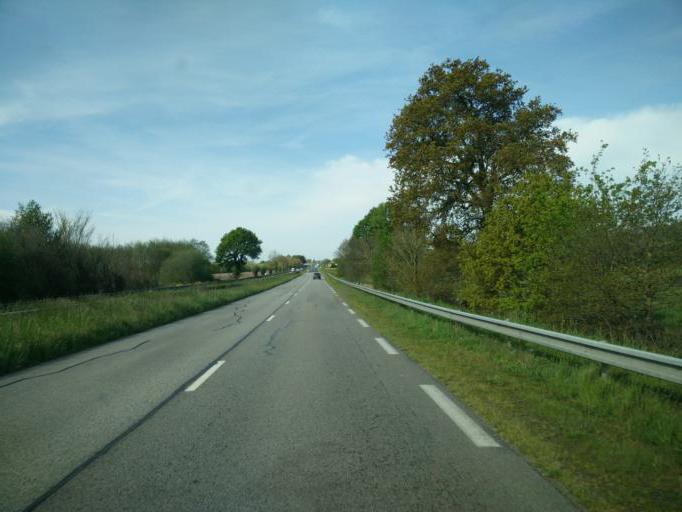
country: FR
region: Lower Normandy
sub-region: Departement de la Manche
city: Le Val-Saint-Pere
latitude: 48.5919
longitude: -1.4171
